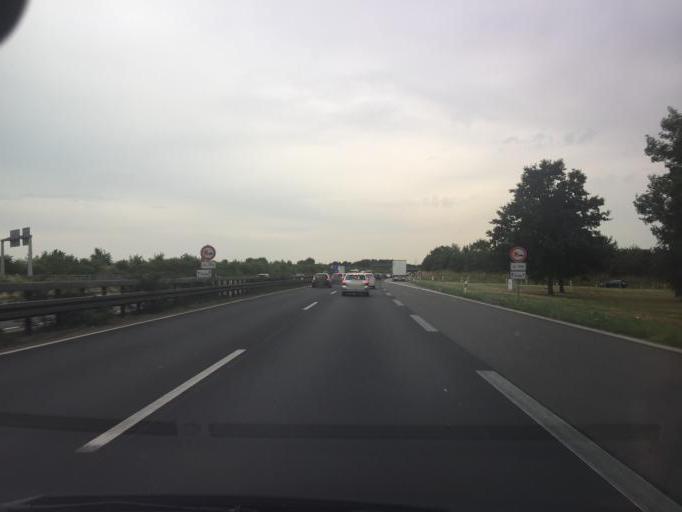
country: DE
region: North Rhine-Westphalia
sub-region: Regierungsbezirk Dusseldorf
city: Viersen
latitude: 51.2099
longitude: 6.3788
